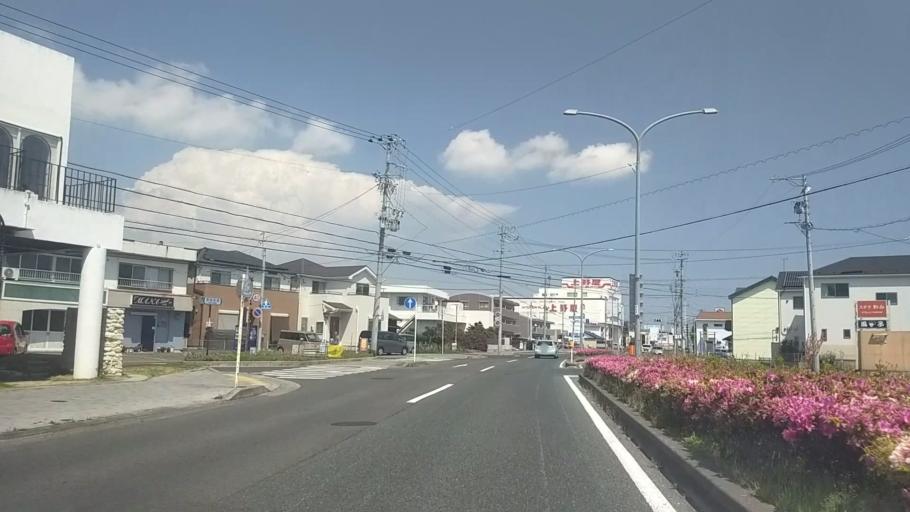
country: JP
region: Shizuoka
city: Hamamatsu
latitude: 34.7002
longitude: 137.7017
